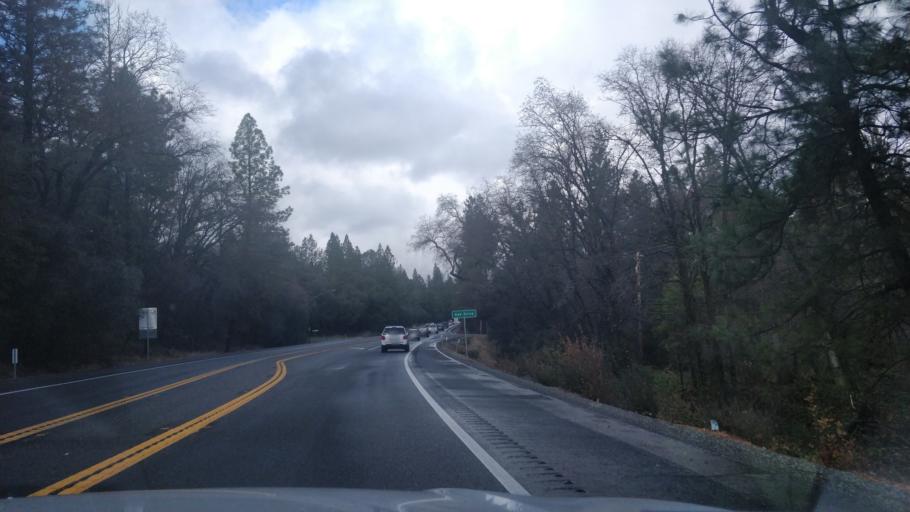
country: US
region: California
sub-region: Nevada County
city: Alta Sierra
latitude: 39.1036
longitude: -121.0855
